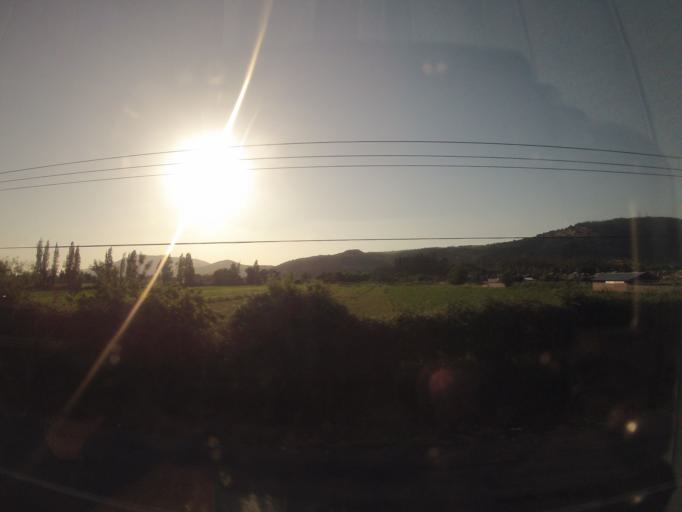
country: CL
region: O'Higgins
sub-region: Provincia de Colchagua
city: Chimbarongo
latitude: -34.6491
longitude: -70.9919
